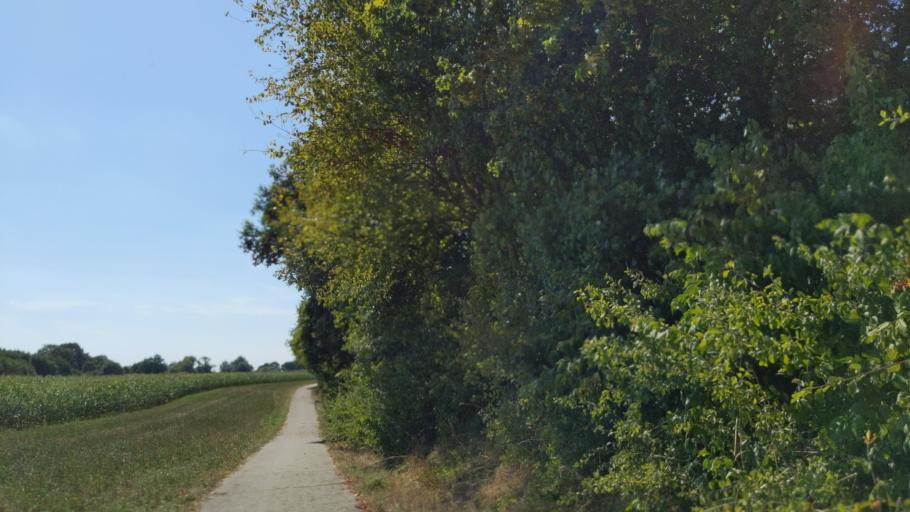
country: DE
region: Mecklenburg-Vorpommern
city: Selmsdorf
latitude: 53.8296
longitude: 10.8637
